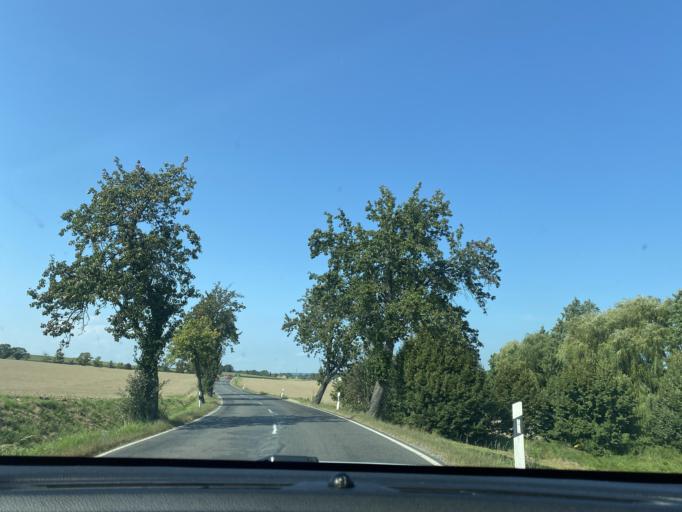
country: DE
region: Saxony
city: Reichenbach
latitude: 51.1793
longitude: 14.7713
